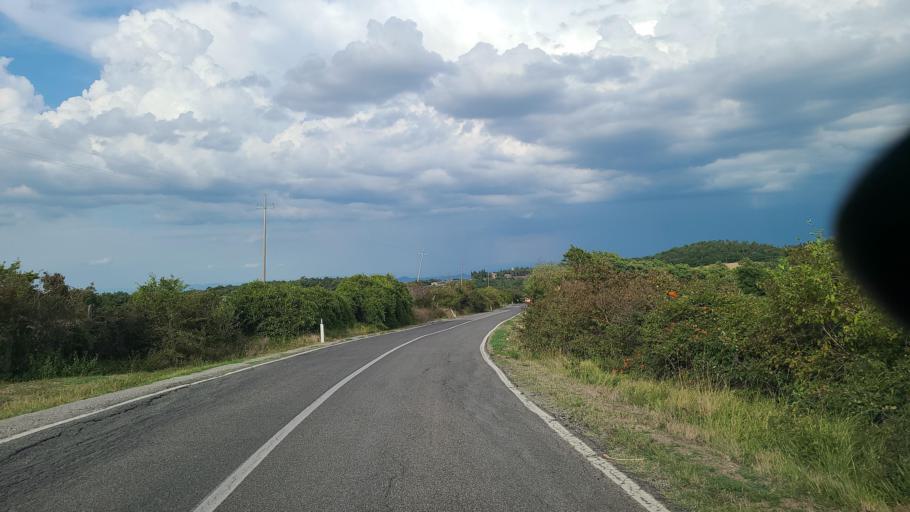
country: IT
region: Tuscany
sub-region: Province of Florence
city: Gambassi Terme
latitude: 43.4837
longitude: 10.9630
